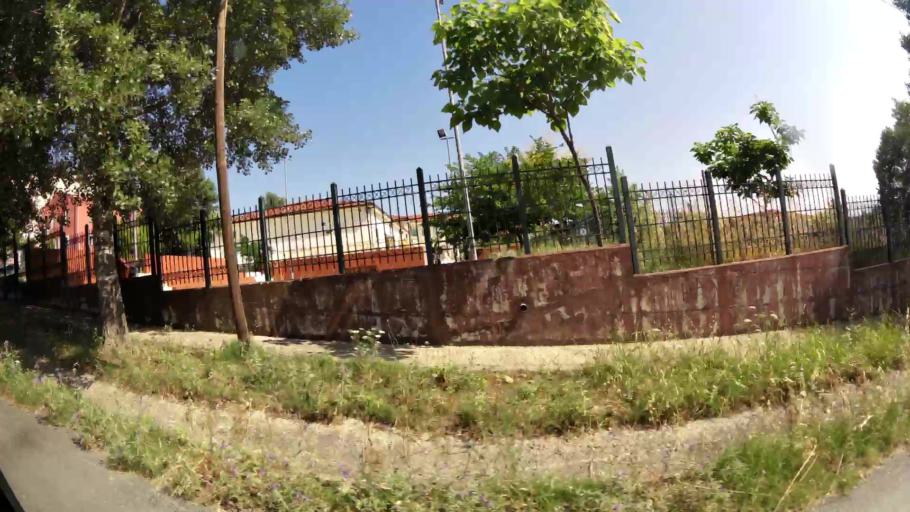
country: GR
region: Central Macedonia
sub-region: Nomos Thessalonikis
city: Peraia
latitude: 40.4953
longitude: 22.9278
